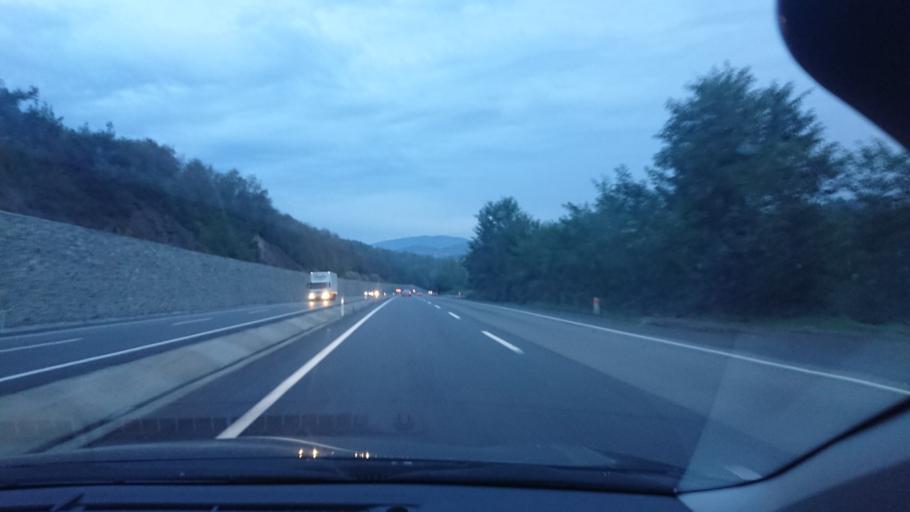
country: TR
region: Zonguldak
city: Beycuma
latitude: 41.3353
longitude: 32.0415
